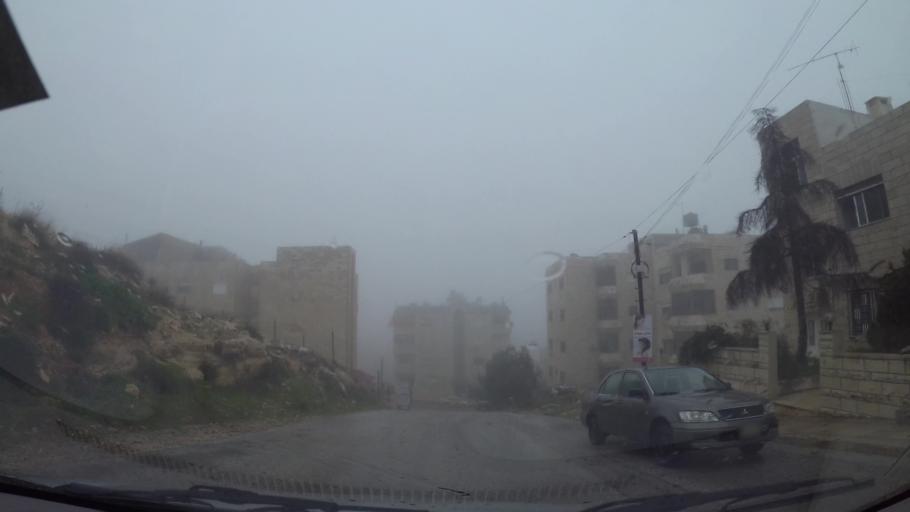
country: JO
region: Amman
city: Al Jubayhah
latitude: 32.0123
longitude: 35.8844
